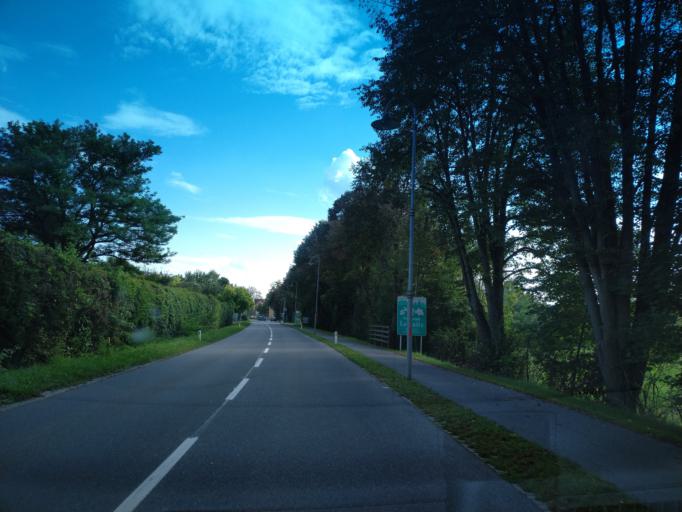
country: AT
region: Styria
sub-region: Politischer Bezirk Leibnitz
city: Leibnitz
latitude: 46.7856
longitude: 15.5343
